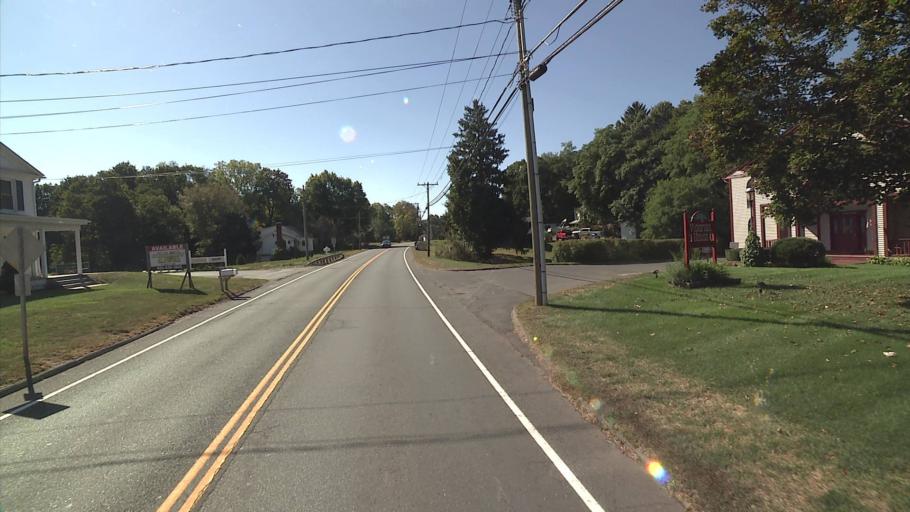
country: US
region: Connecticut
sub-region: Tolland County
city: Rockville
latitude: 41.8727
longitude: -72.4634
